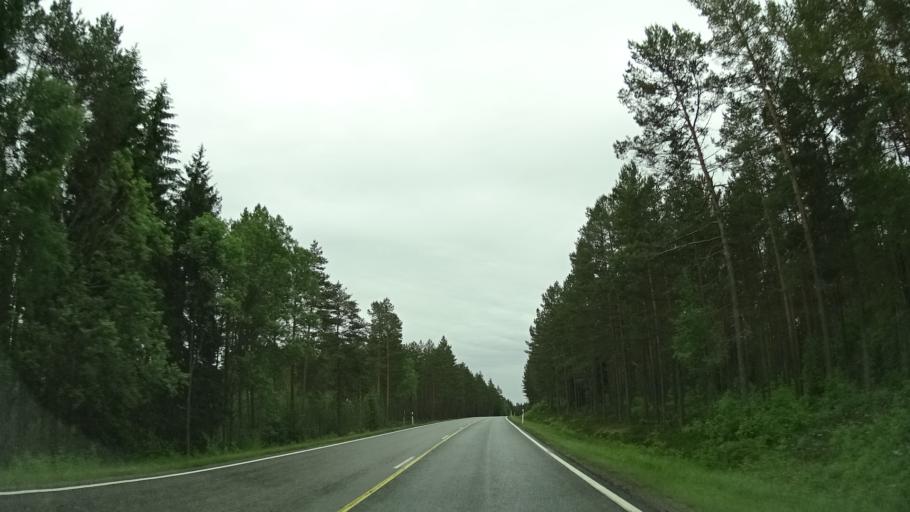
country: FI
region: Varsinais-Suomi
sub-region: Salo
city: Pernioe
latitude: 60.1113
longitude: 23.2136
